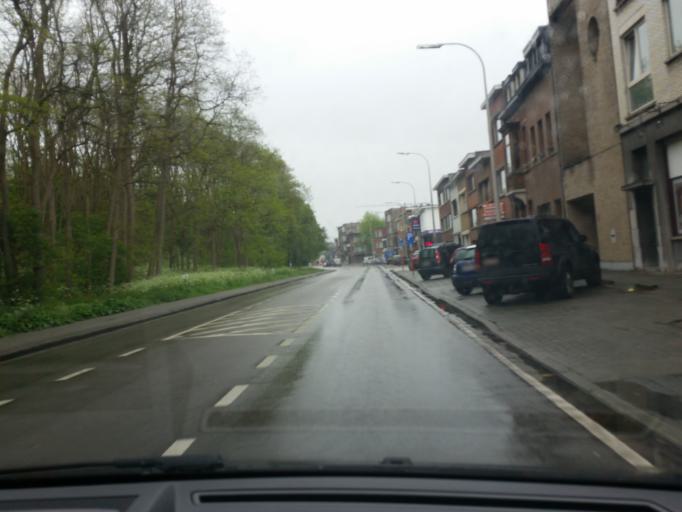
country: BE
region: Flanders
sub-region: Provincie Antwerpen
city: Mortsel
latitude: 51.1727
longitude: 4.4398
